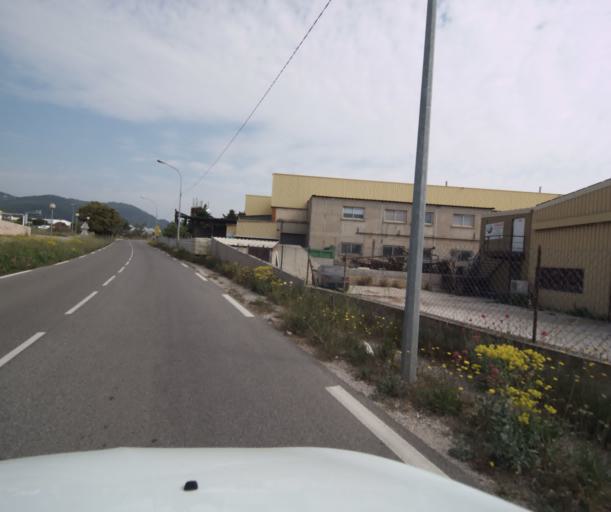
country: FR
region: Provence-Alpes-Cote d'Azur
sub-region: Departement du Var
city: La Farlede
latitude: 43.1497
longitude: 6.0378
